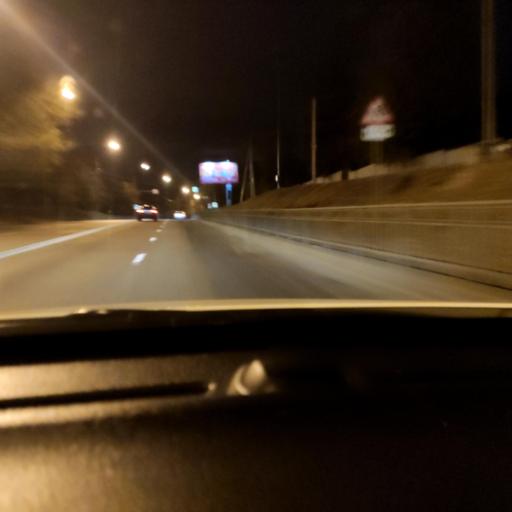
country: RU
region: Voronezj
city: Voronezh
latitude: 51.6340
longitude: 39.1985
